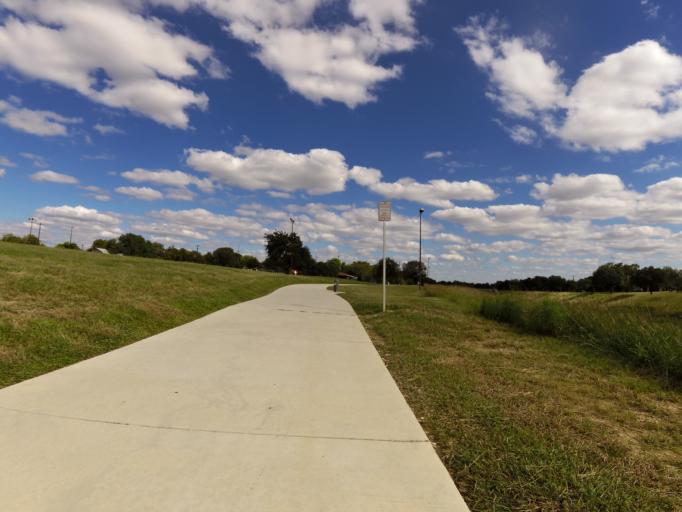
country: US
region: Texas
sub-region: Bexar County
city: San Antonio
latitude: 29.4138
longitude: -98.5234
